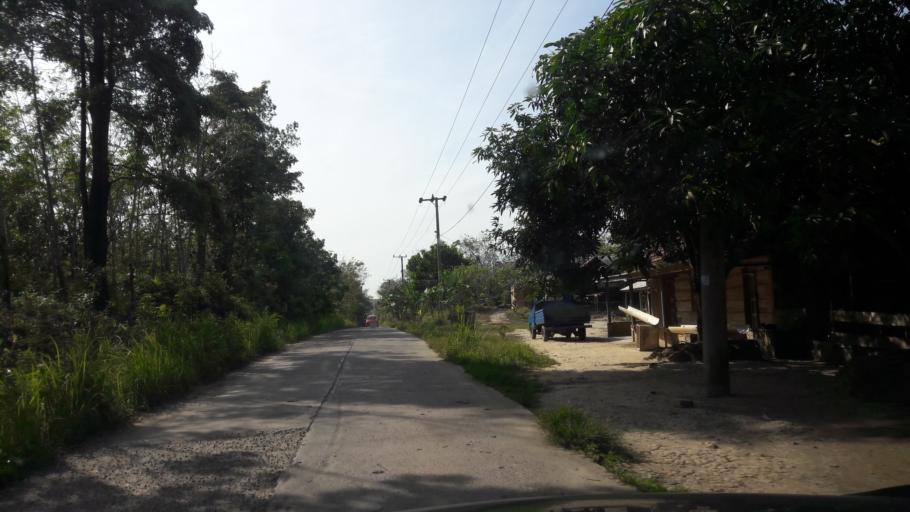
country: ID
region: South Sumatra
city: Gunungmenang
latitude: -3.3141
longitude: 104.0118
